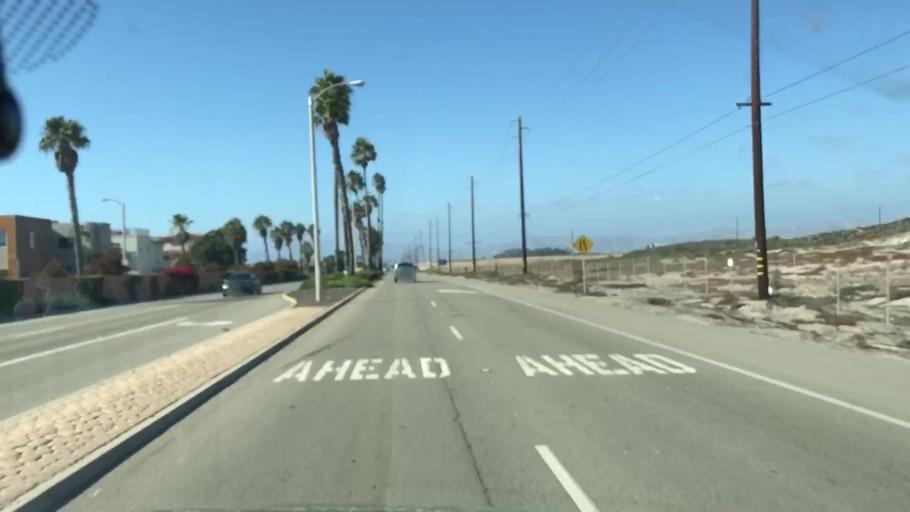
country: US
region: California
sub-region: Ventura County
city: Oxnard Shores
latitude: 34.1946
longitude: -119.2407
